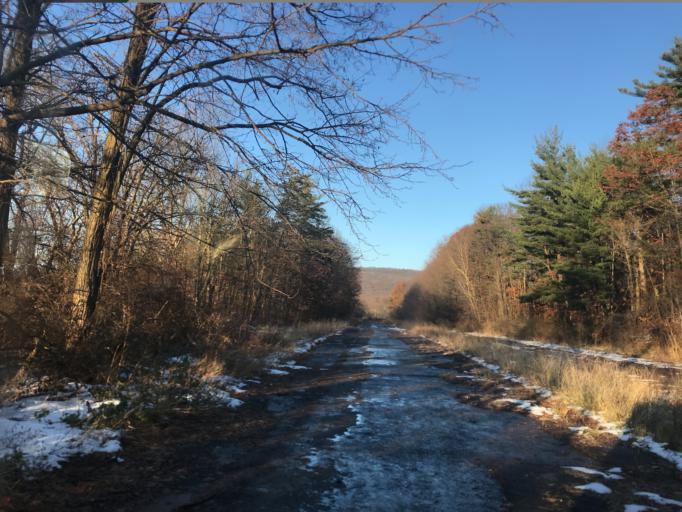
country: US
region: Pennsylvania
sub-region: Bedford County
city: Earlston
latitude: 40.0103
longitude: -78.2160
